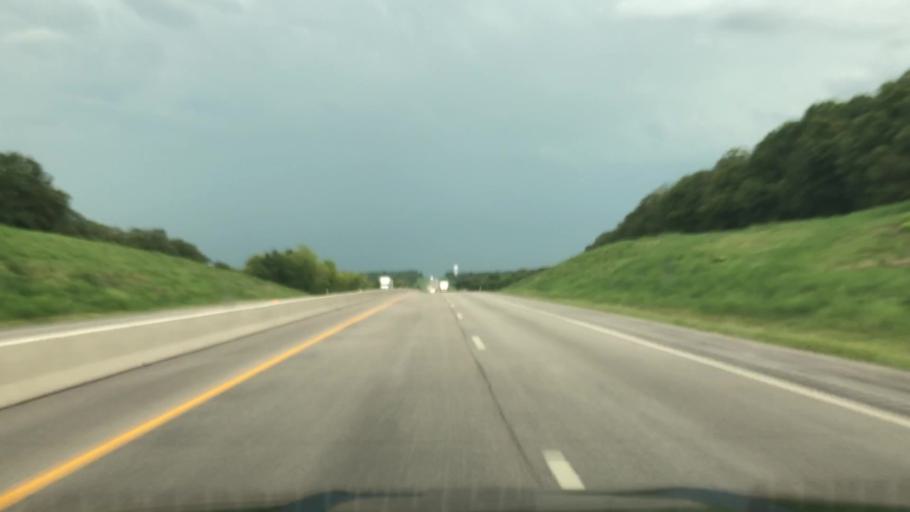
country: US
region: Oklahoma
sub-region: Rogers County
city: Justice
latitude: 36.3334
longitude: -95.5183
